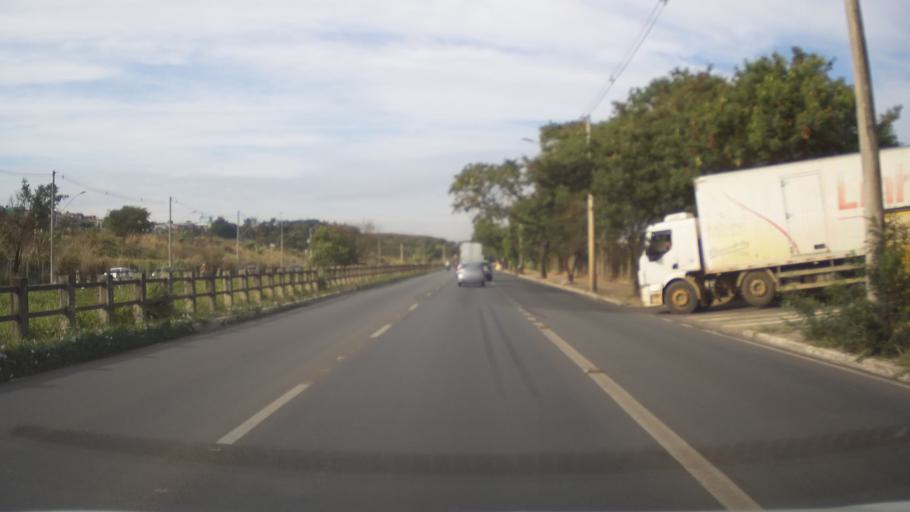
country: BR
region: Minas Gerais
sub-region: Contagem
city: Contagem
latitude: -19.8911
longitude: -44.0392
